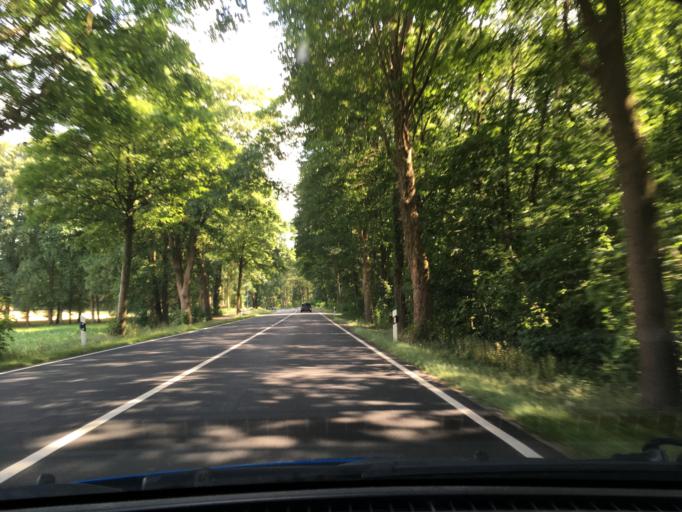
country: DE
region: Lower Saxony
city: Welle
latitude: 53.2272
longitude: 9.8063
